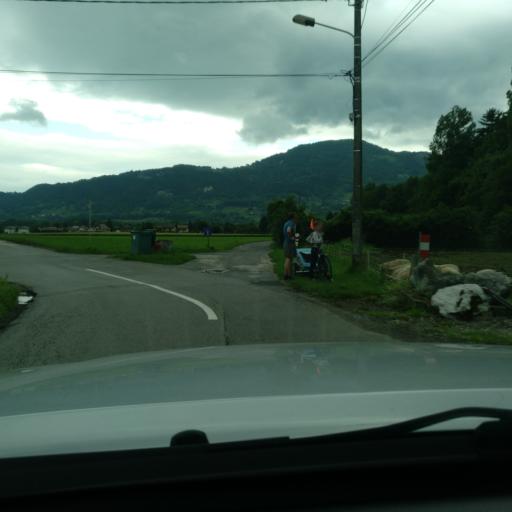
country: FR
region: Rhone-Alpes
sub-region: Departement de la Haute-Savoie
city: Amancy
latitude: 46.0832
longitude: 6.3467
